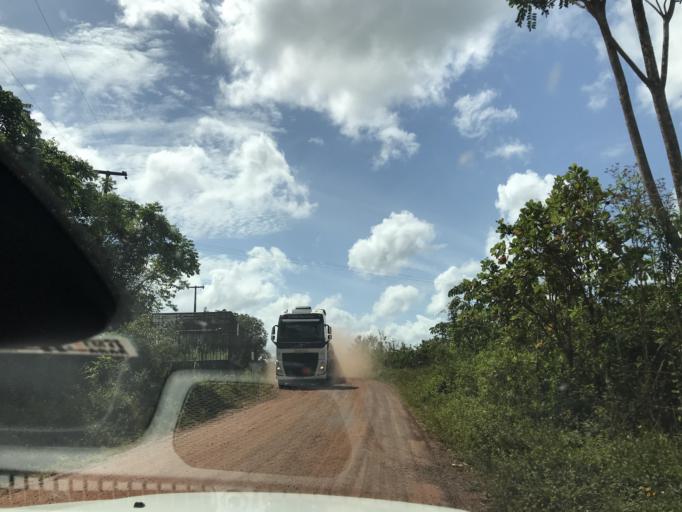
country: BR
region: Bahia
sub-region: Entre Rios
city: Entre Rios
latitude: -12.1645
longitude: -38.0747
